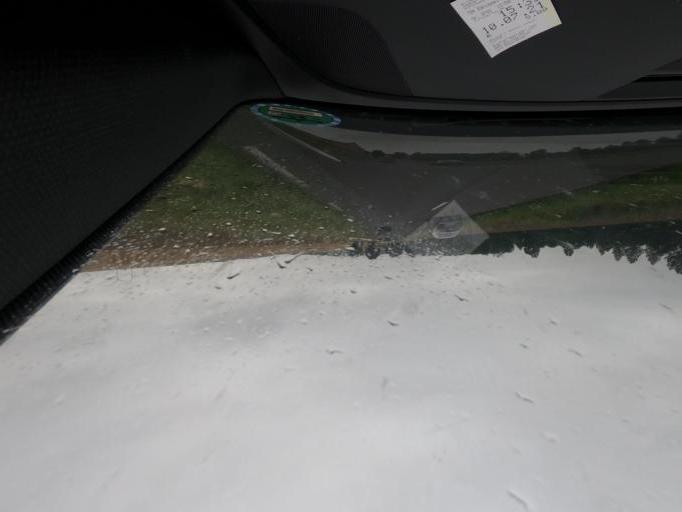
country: FR
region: Picardie
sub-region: Departement de la Somme
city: Moreuil
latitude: 49.8168
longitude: 2.4812
